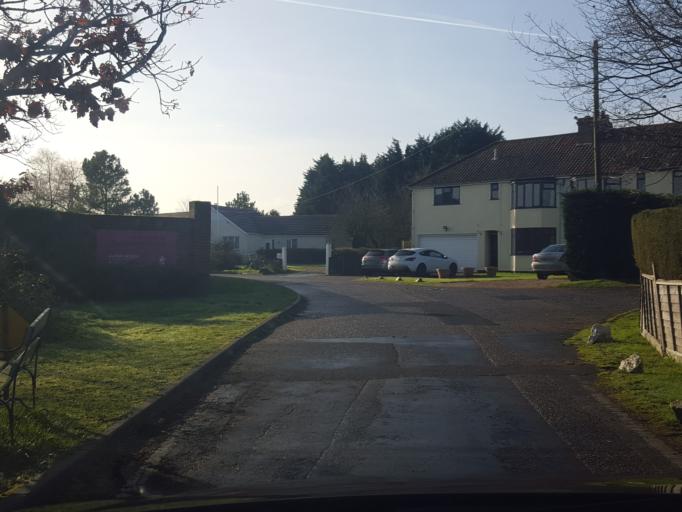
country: GB
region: England
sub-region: Essex
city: Eight Ash Green
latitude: 51.8927
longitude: 0.8229
